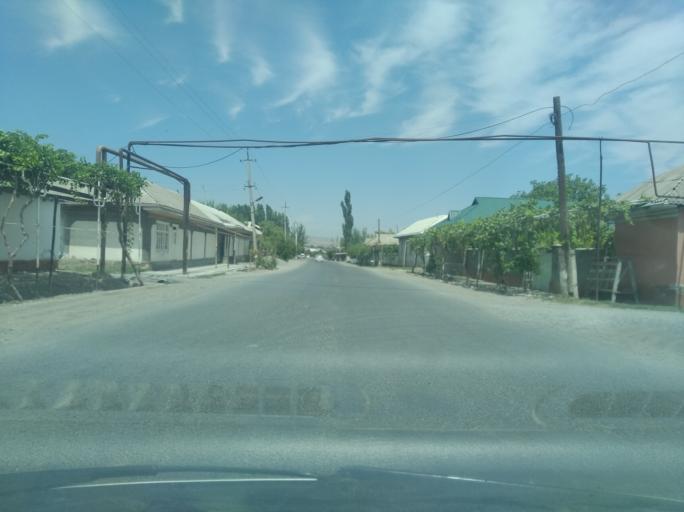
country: KG
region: Osh
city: Aravan
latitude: 40.6164
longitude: 72.4546
